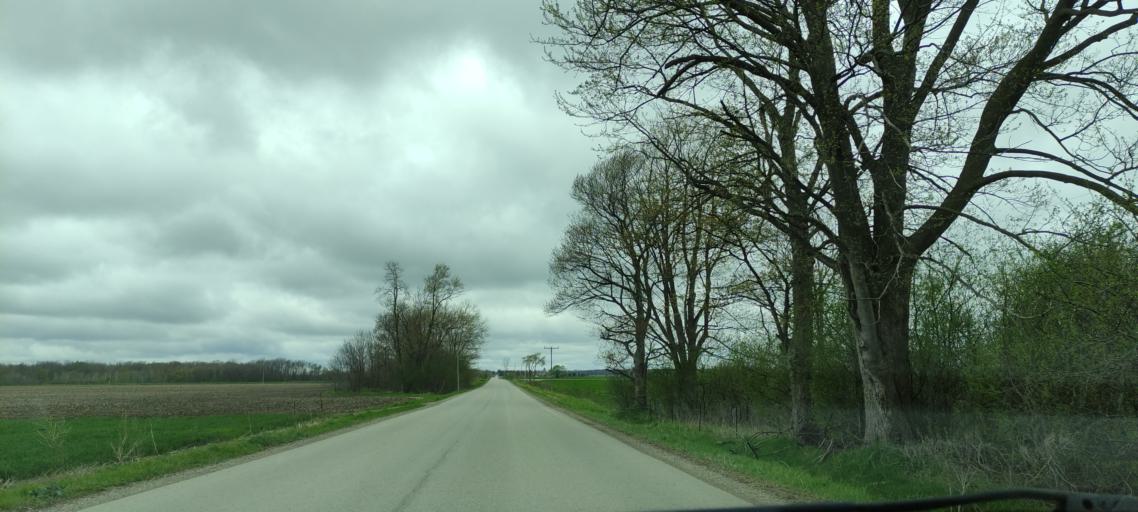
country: CA
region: Ontario
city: Stratford
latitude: 43.4268
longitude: -80.9602
